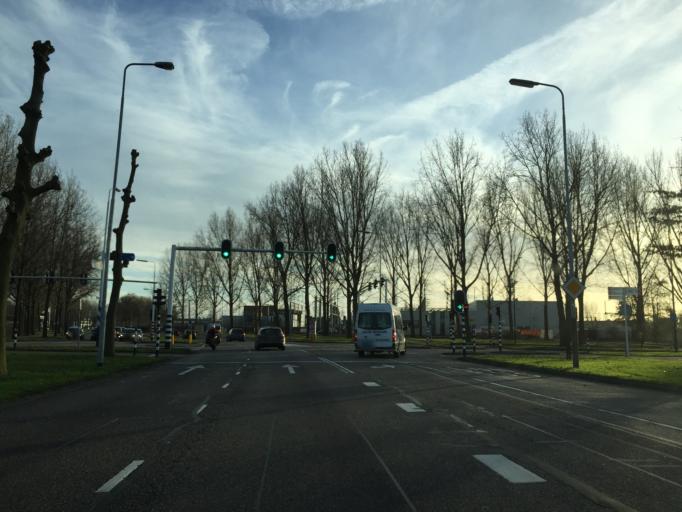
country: NL
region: North Brabant
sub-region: Gemeente 's-Hertogenbosch
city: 's-Hertogenbosch
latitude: 51.7122
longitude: 5.2981
